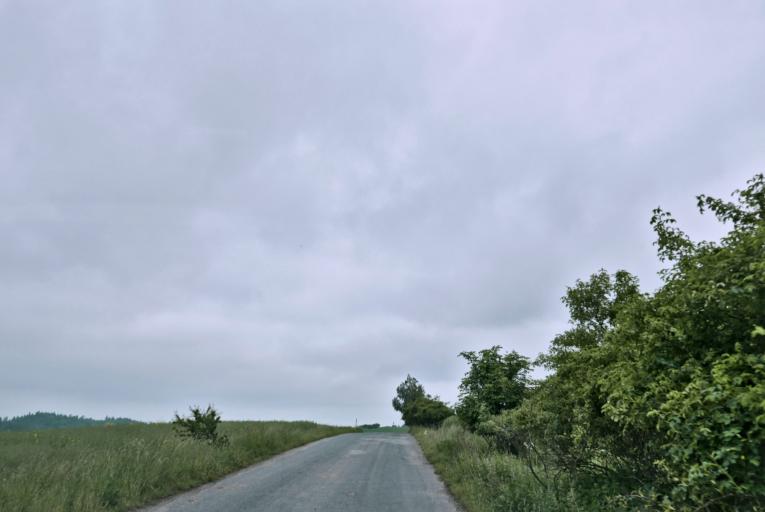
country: CZ
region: Plzensky
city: Zihle
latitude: 50.0147
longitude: 13.3309
